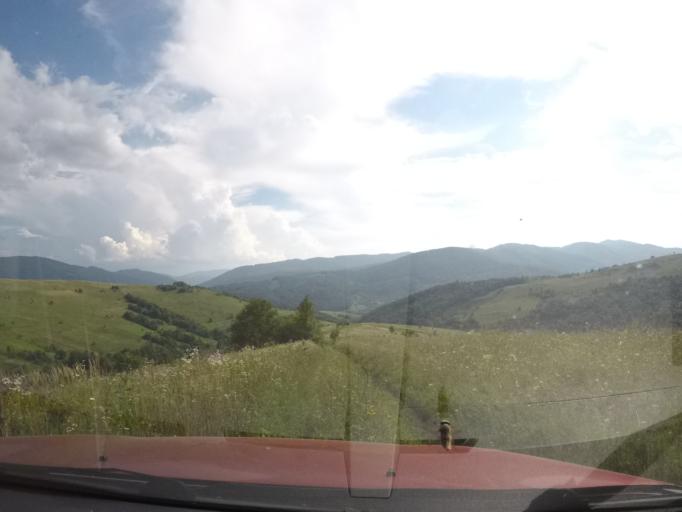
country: UA
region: Zakarpattia
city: Velykyi Bereznyi
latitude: 49.0278
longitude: 22.6403
